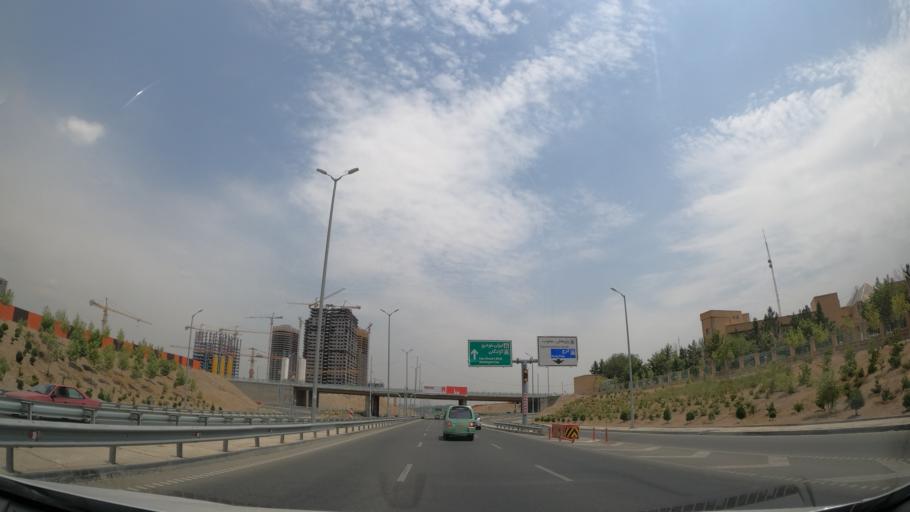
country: IR
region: Tehran
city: Shahr-e Qods
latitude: 35.7496
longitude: 51.1740
